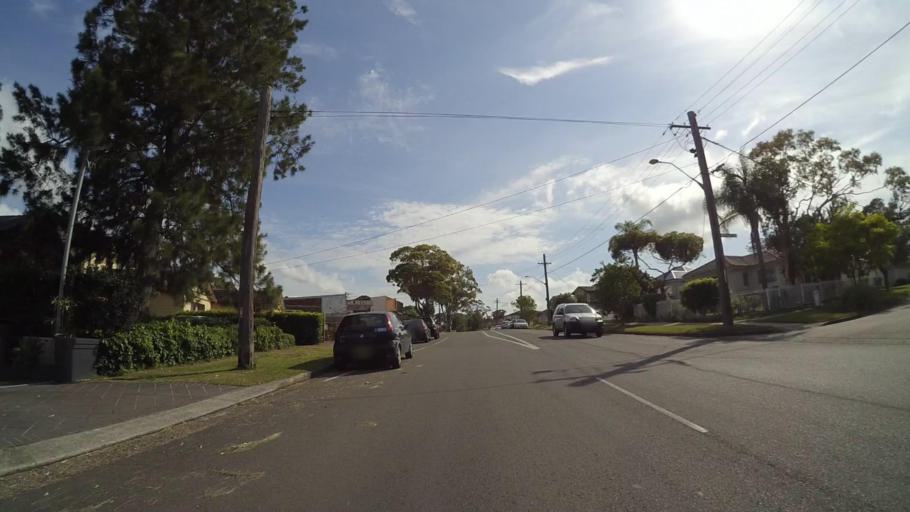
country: AU
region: New South Wales
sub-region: Sutherland Shire
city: Caringbah
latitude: -34.0512
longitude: 151.1156
